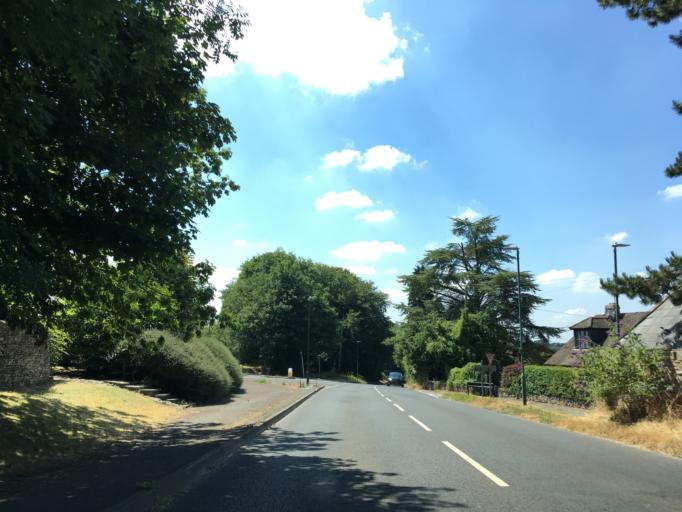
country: GB
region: England
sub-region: Gloucestershire
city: Chalford
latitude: 51.7356
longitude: -2.1628
